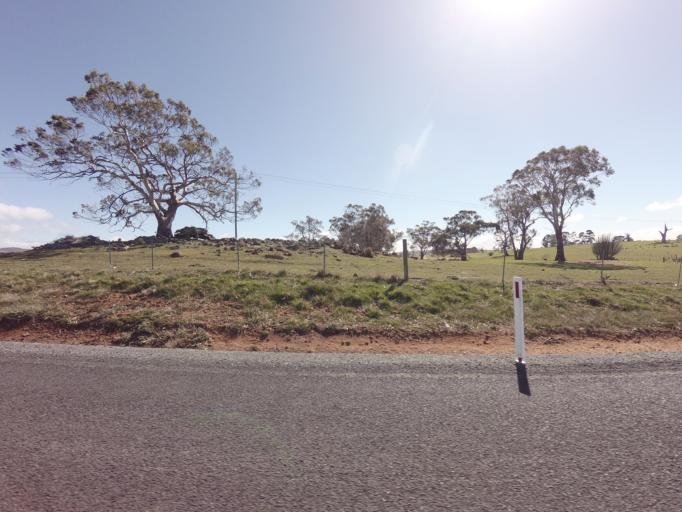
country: AU
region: Tasmania
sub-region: Northern Midlands
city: Evandale
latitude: -41.9081
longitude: 147.3866
